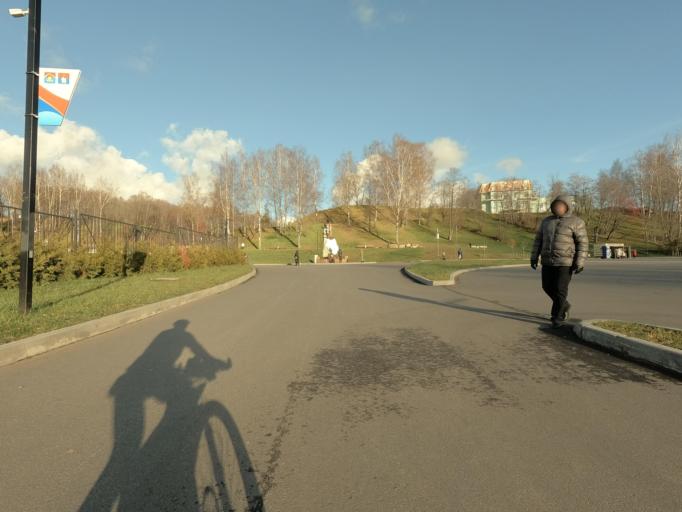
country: RU
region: Leningrad
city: Vsevolozhsk
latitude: 60.0319
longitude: 30.6430
